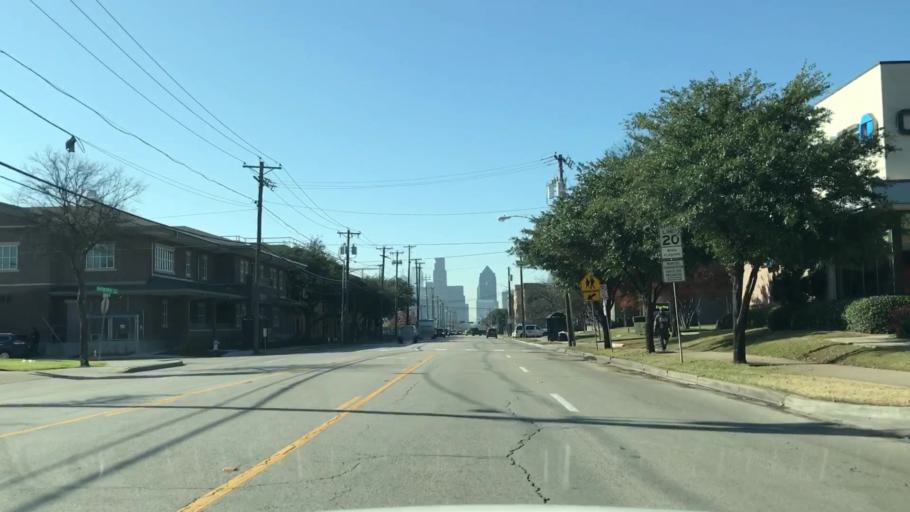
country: US
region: Texas
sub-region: Dallas County
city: Highland Park
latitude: 32.8052
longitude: -96.7778
